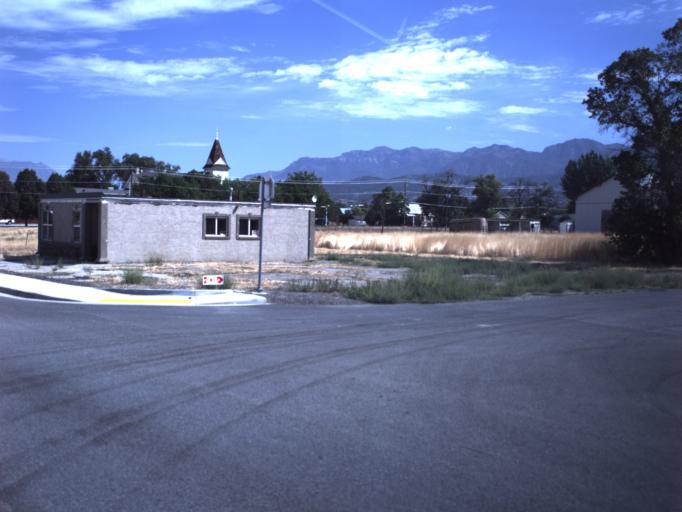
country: US
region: Utah
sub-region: Juab County
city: Nephi
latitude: 39.5558
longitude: -111.8638
